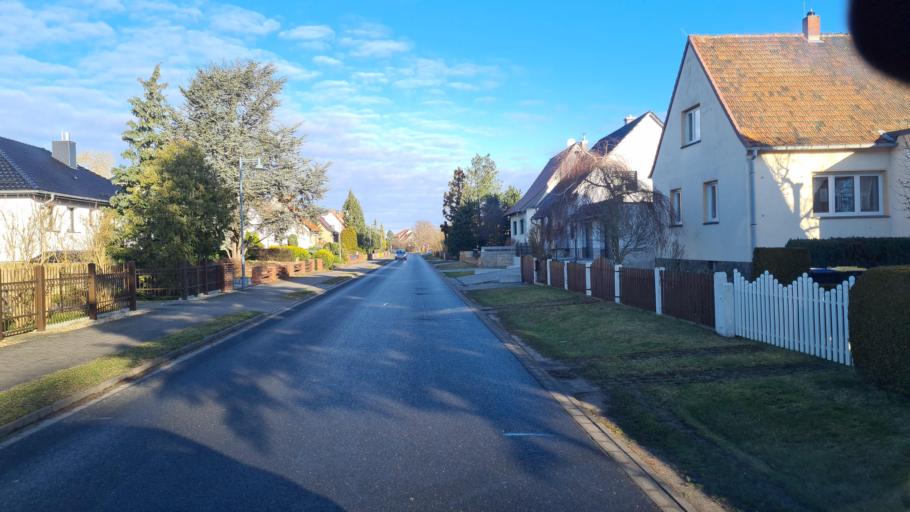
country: DE
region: Brandenburg
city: Herzberg
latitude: 51.6922
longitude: 13.2251
